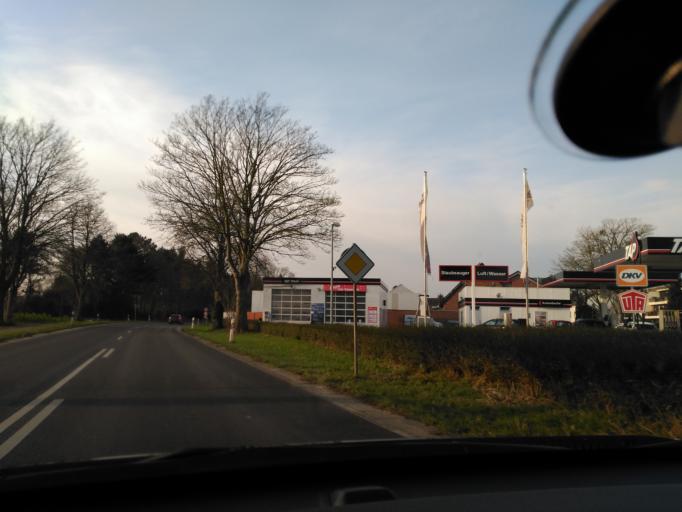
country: DE
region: North Rhine-Westphalia
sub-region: Regierungsbezirk Dusseldorf
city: Monchengladbach
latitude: 51.1473
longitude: 6.3713
